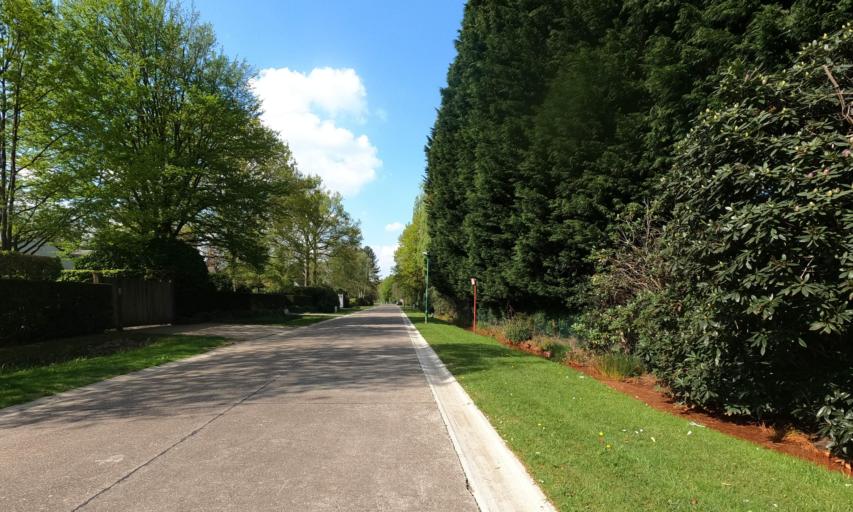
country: BE
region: Flanders
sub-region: Provincie Antwerpen
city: Schilde
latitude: 51.2450
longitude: 4.6124
